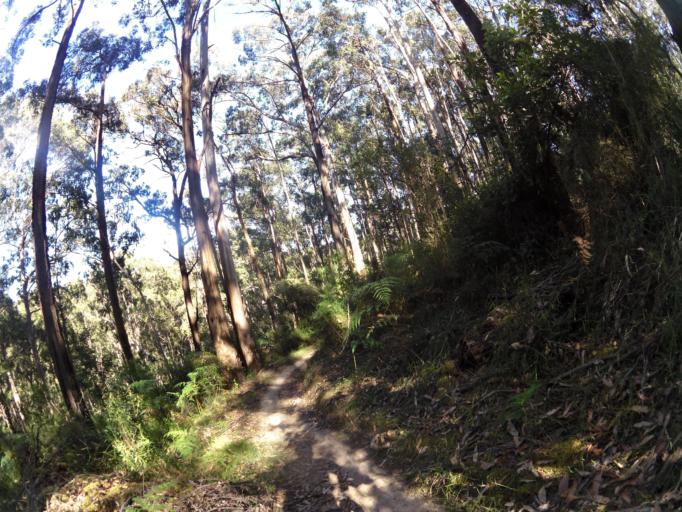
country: AU
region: Victoria
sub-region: Colac-Otway
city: Apollo Bay
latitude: -38.5456
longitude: 143.7333
